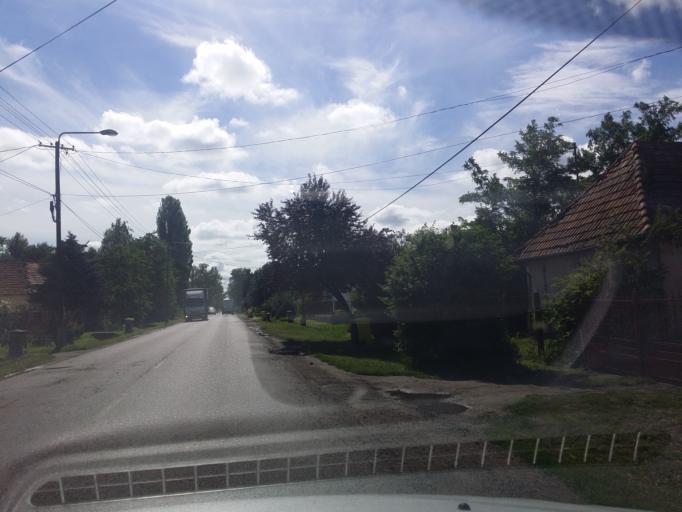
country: HU
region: Jasz-Nagykun-Szolnok
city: Jaszszentandras
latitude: 47.6458
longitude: 20.1676
